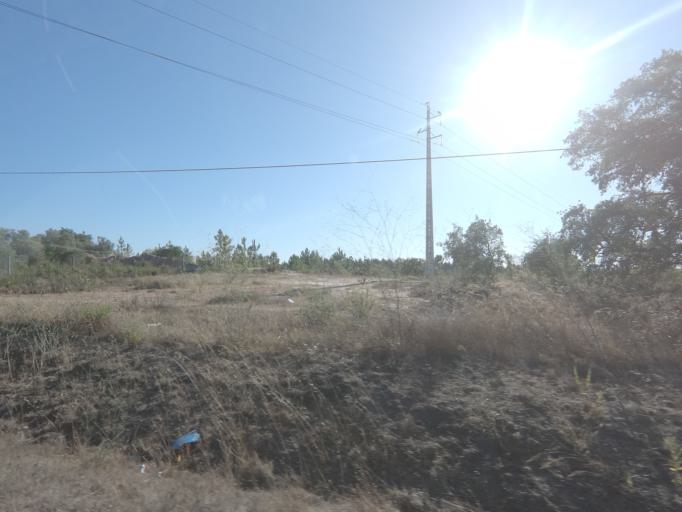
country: PT
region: Setubal
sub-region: Moita
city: Moita
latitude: 38.6220
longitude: -8.9582
